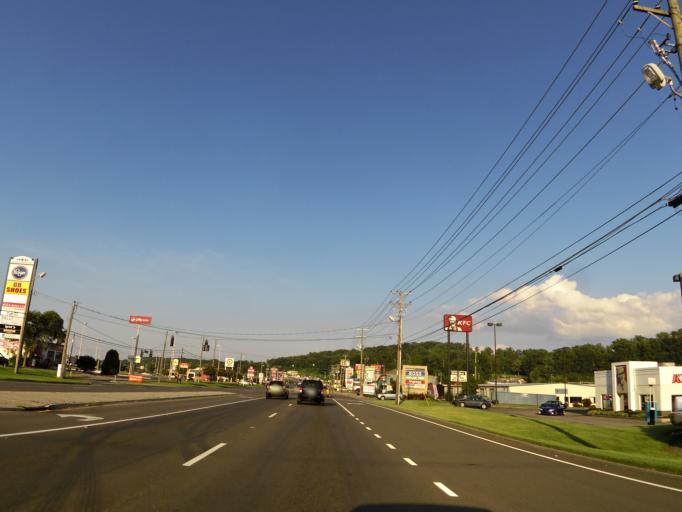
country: US
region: Tennessee
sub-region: Knox County
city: Knoxville
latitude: 36.0069
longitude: -84.0244
